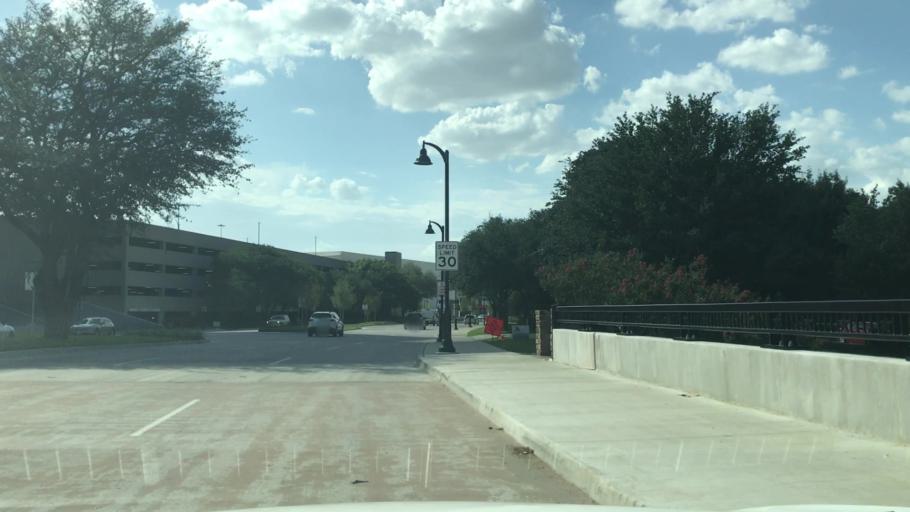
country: US
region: Texas
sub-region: Dallas County
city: Irving
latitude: 32.8711
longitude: -96.9421
